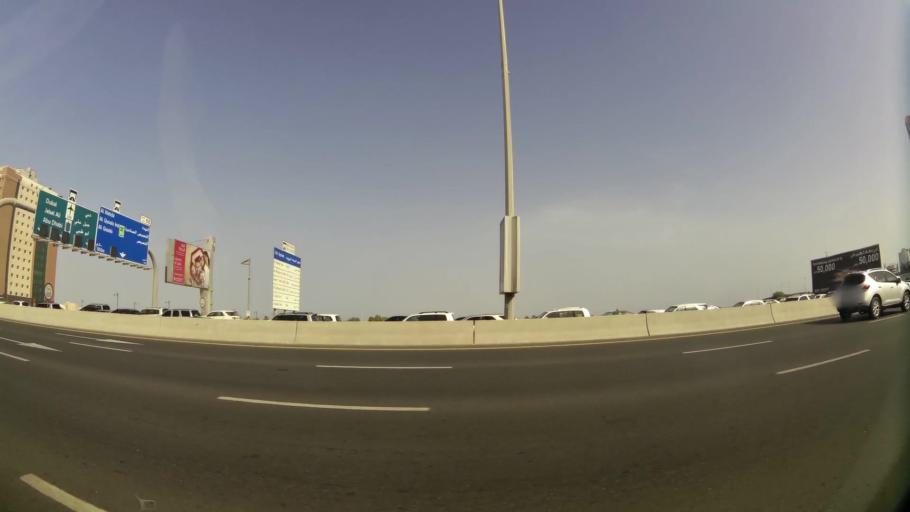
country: AE
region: Ash Shariqah
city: Sharjah
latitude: 25.2987
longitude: 55.3624
